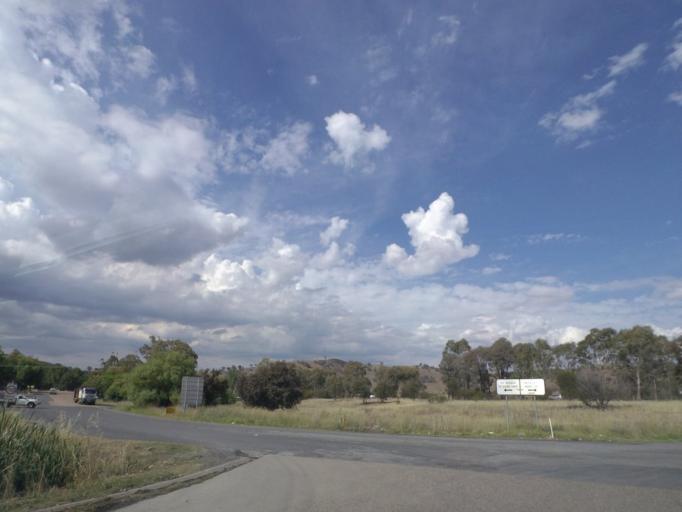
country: AU
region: New South Wales
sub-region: Gundagai
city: Gundagai
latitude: -35.0033
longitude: 148.1108
